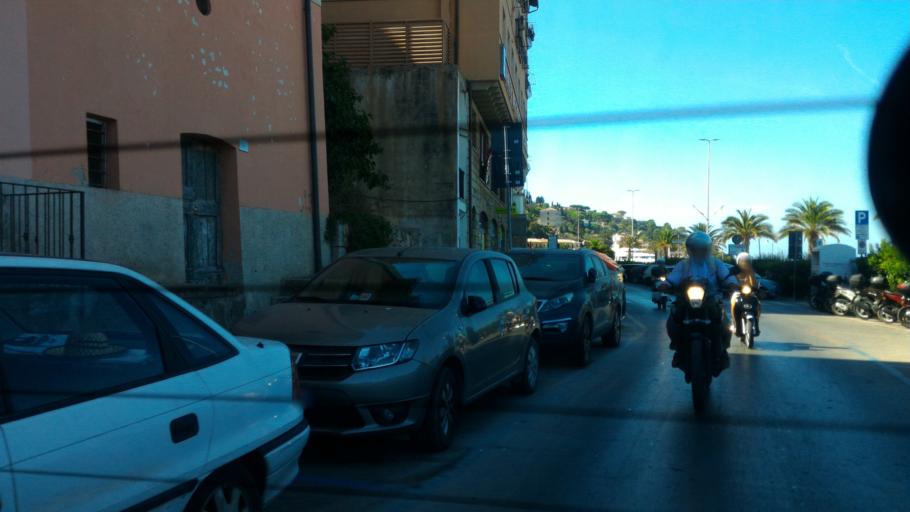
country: IT
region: Tuscany
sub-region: Provincia di Grosseto
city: Porto Santo Stefano
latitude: 42.4387
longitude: 11.1193
